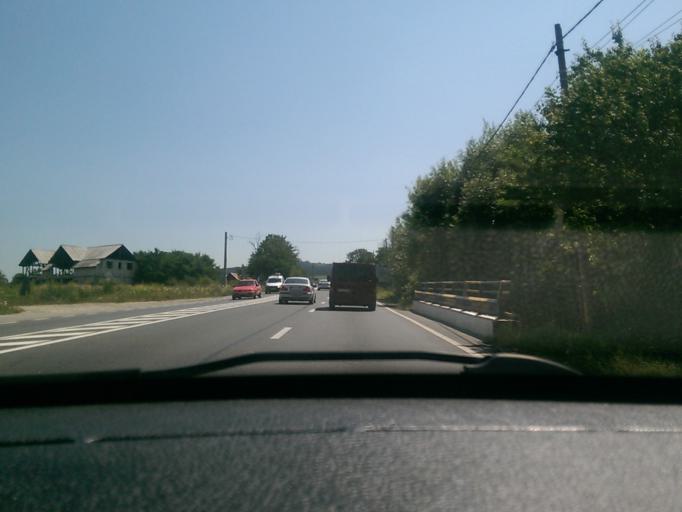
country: RO
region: Cluj
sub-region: Comuna Feleacu
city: Feleacu
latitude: 46.7311
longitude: 23.5970
